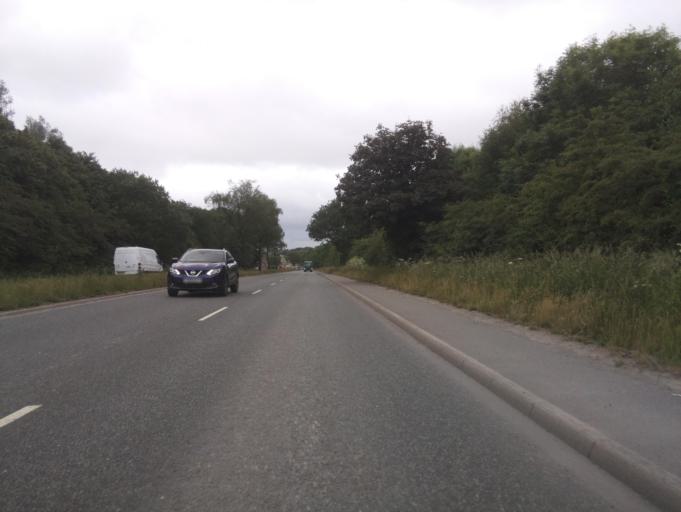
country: GB
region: England
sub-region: Leicestershire
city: Markfield
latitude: 52.7012
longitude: -1.3098
